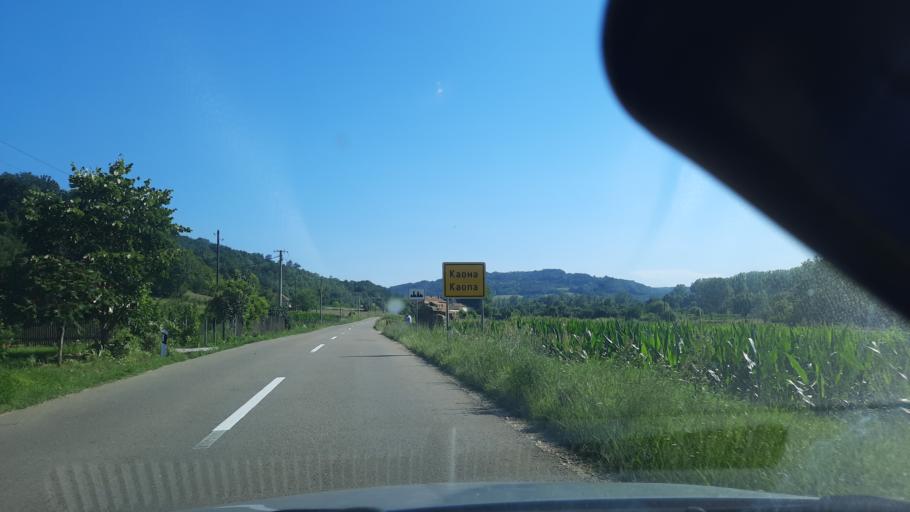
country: RS
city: Turija
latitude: 44.5035
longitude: 21.6321
